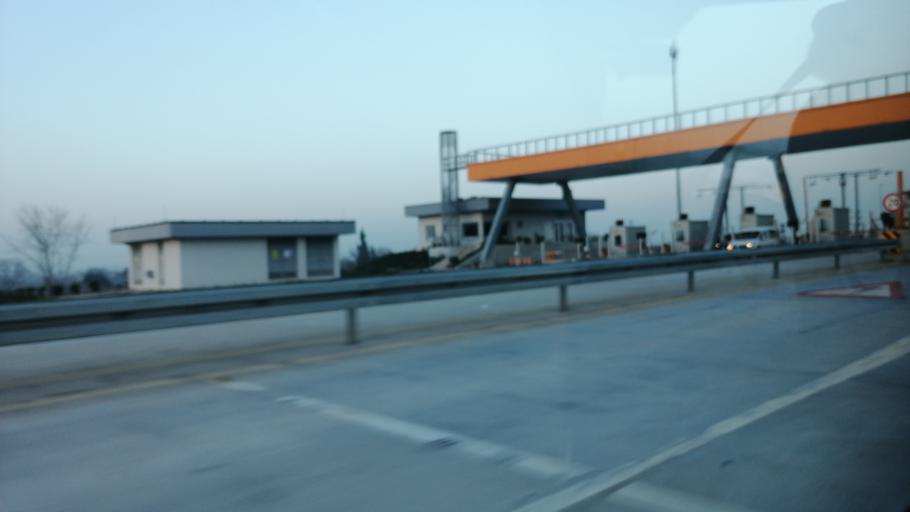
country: TR
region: Yalova
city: Altinova
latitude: 40.6964
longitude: 29.4748
